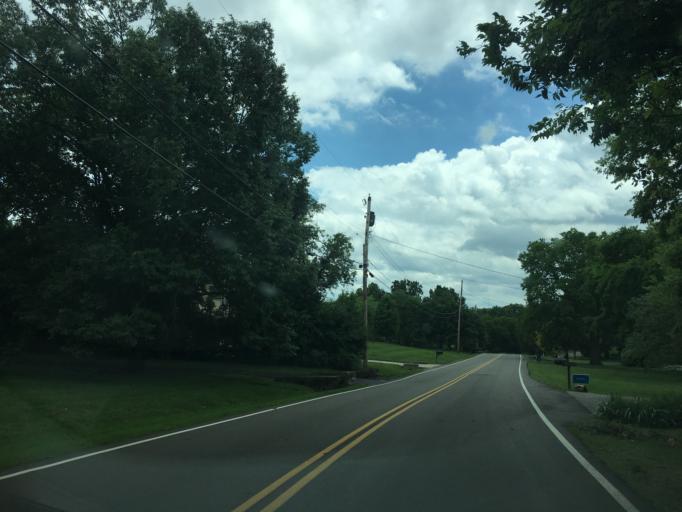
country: US
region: Tennessee
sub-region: Davidson County
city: Belle Meade
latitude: 36.0880
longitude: -86.8410
